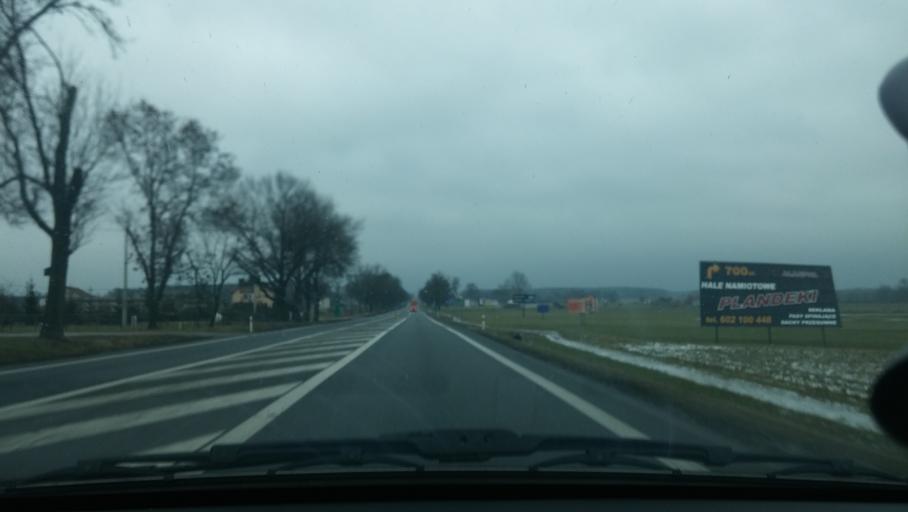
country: PL
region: Masovian Voivodeship
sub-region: Powiat siedlecki
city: Kotun
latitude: 52.1974
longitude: 22.0588
